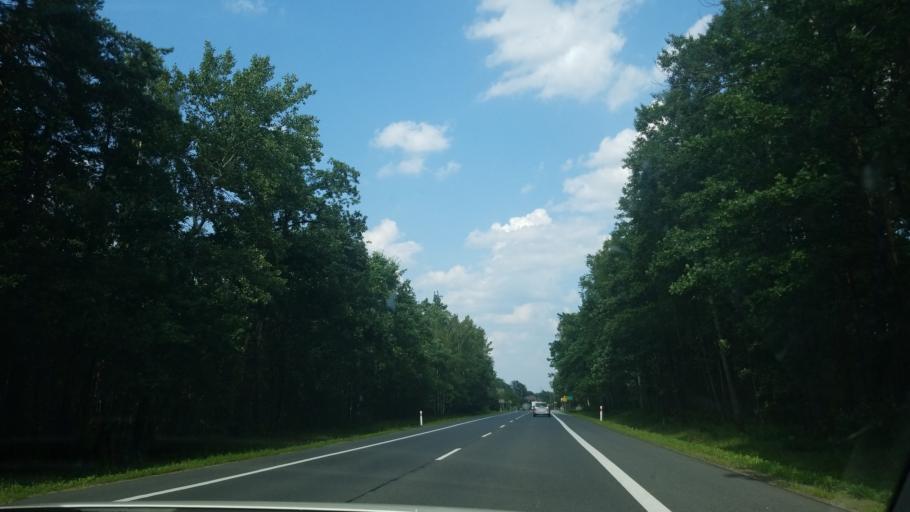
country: PL
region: Subcarpathian Voivodeship
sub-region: Powiat nizanski
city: Wolka Tanewska
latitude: 50.5665
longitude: 22.2510
